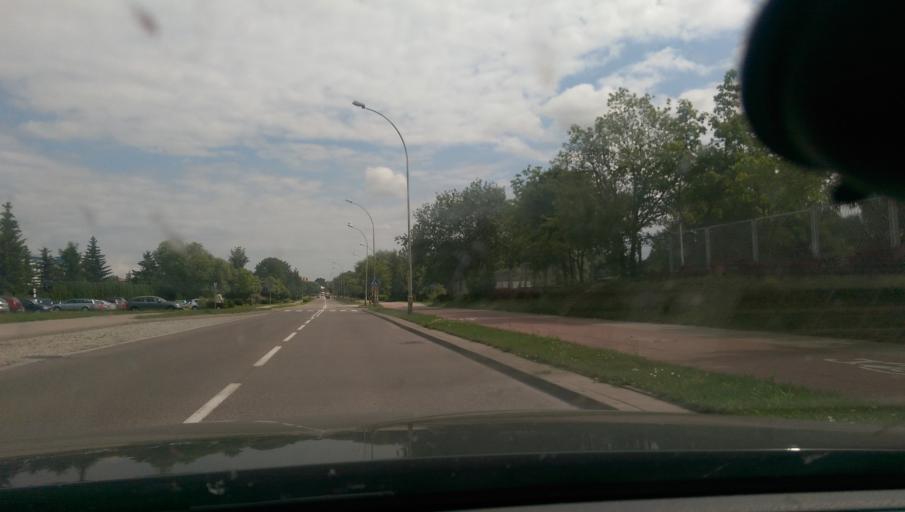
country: PL
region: Podlasie
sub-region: Suwalki
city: Suwalki
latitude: 54.1048
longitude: 22.9111
